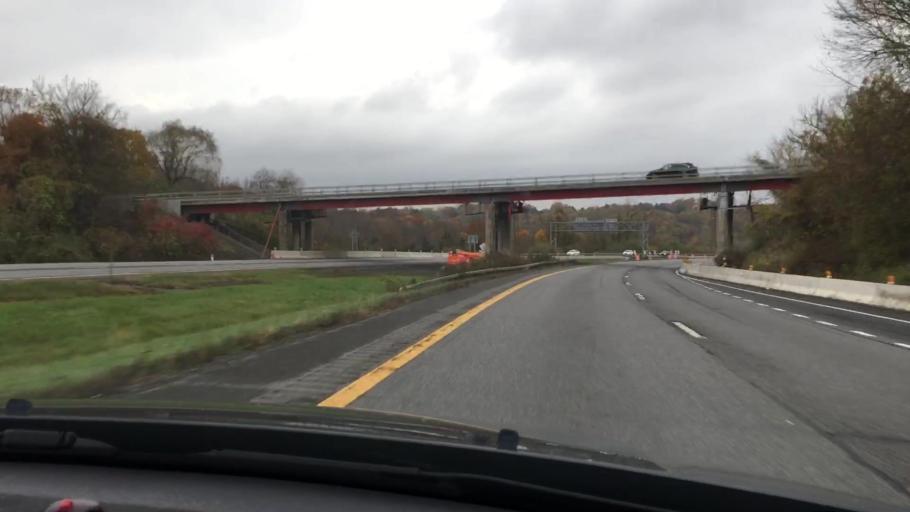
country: US
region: New York
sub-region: Putnam County
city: Brewster
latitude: 41.3917
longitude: -73.5991
